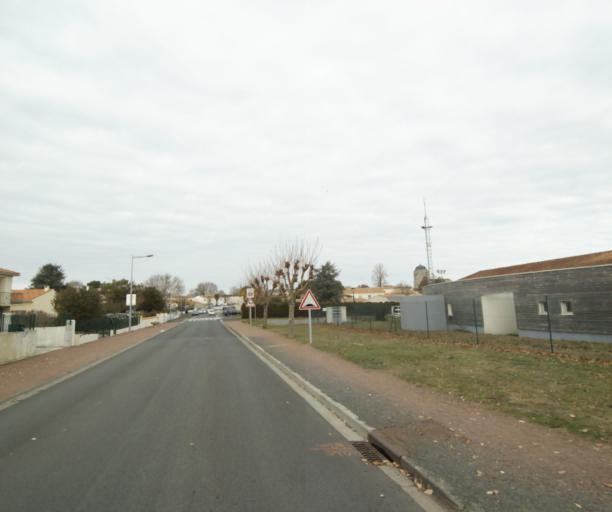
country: FR
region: Poitou-Charentes
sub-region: Departement de la Charente-Maritime
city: Corme-Royal
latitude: 45.7433
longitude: -0.8138
